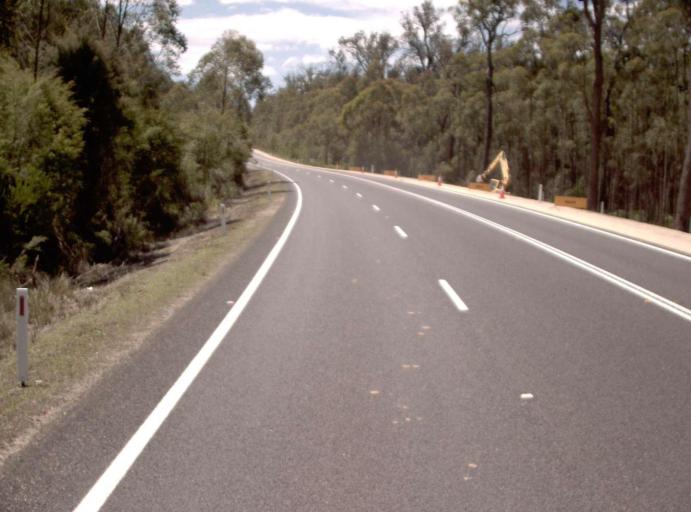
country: AU
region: New South Wales
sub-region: Bombala
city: Bombala
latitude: -37.6262
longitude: 148.8891
